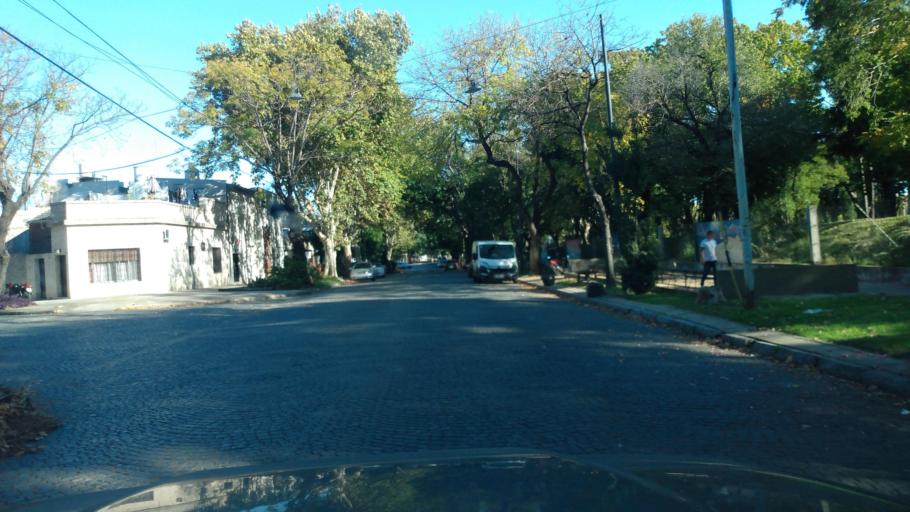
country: AR
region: Buenos Aires F.D.
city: Villa Santa Rita
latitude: -34.5940
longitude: -58.4702
